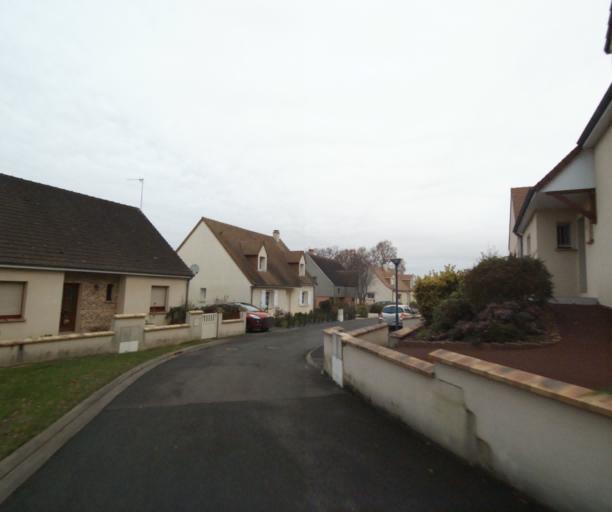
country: FR
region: Pays de la Loire
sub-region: Departement de la Sarthe
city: Coulaines
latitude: 48.0220
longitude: 0.2131
